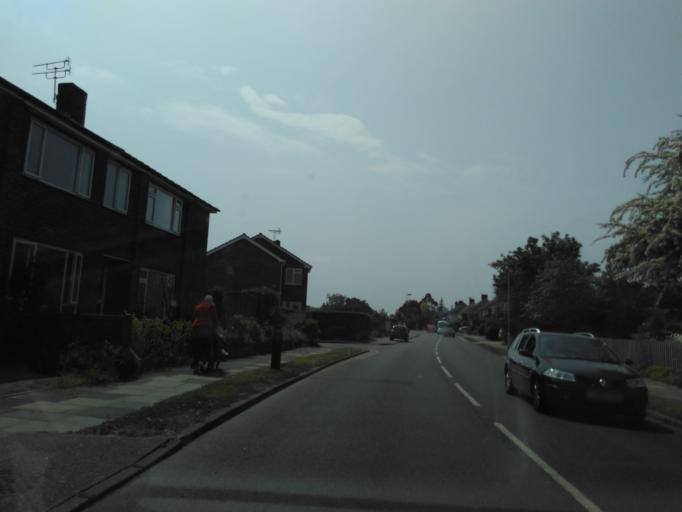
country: GB
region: England
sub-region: Kent
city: Canterbury
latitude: 51.2893
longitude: 1.0876
